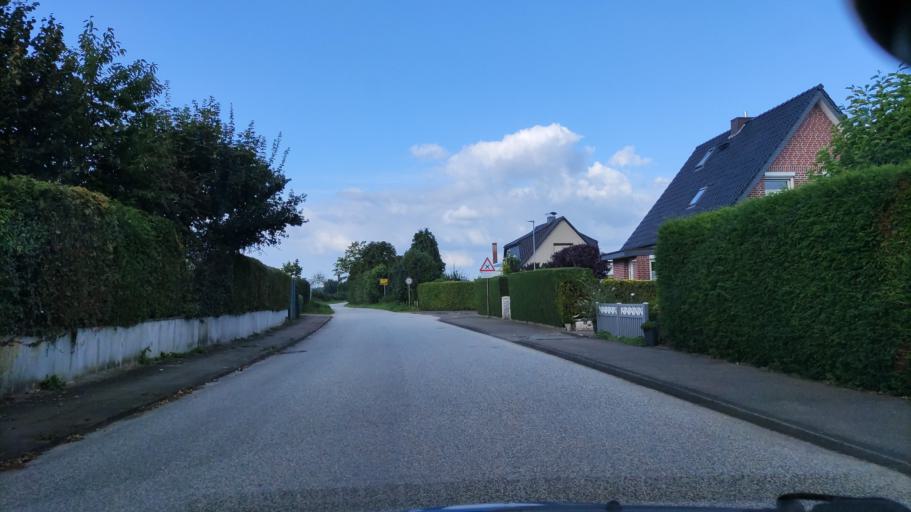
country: DE
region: Schleswig-Holstein
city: Alt Molln
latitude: 53.6090
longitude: 10.6412
